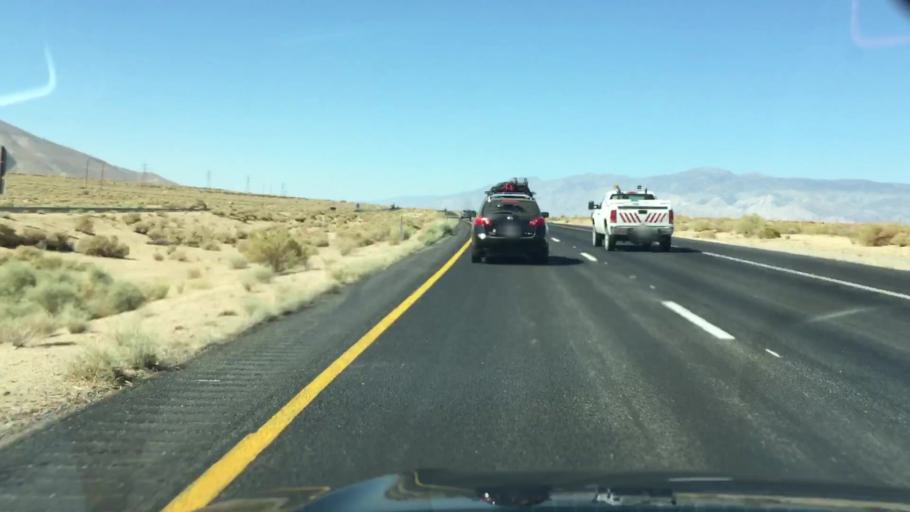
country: US
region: California
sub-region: Inyo County
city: Lone Pine
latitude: 36.3790
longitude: -118.0236
